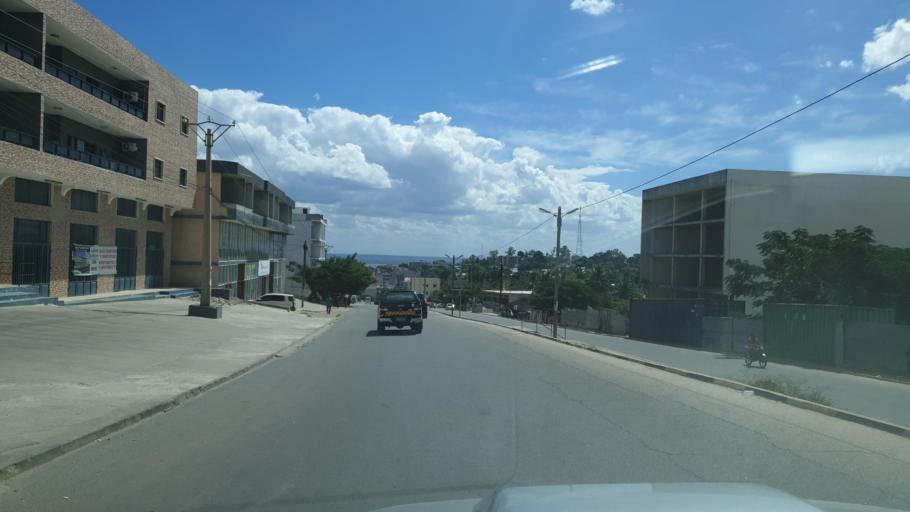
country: MZ
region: Nampula
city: Nacala
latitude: -14.5461
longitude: 40.6842
